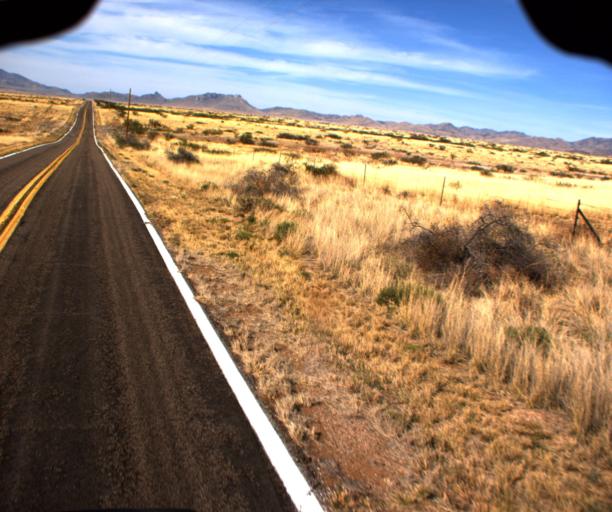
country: US
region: Arizona
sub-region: Cochise County
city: Willcox
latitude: 31.9557
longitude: -109.4772
